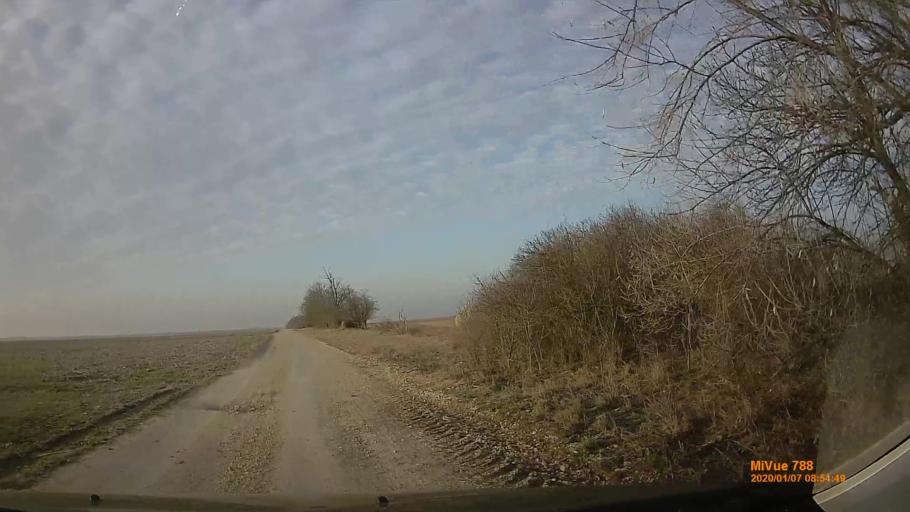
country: HU
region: Gyor-Moson-Sopron
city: Rajka
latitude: 47.9932
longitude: 17.1766
